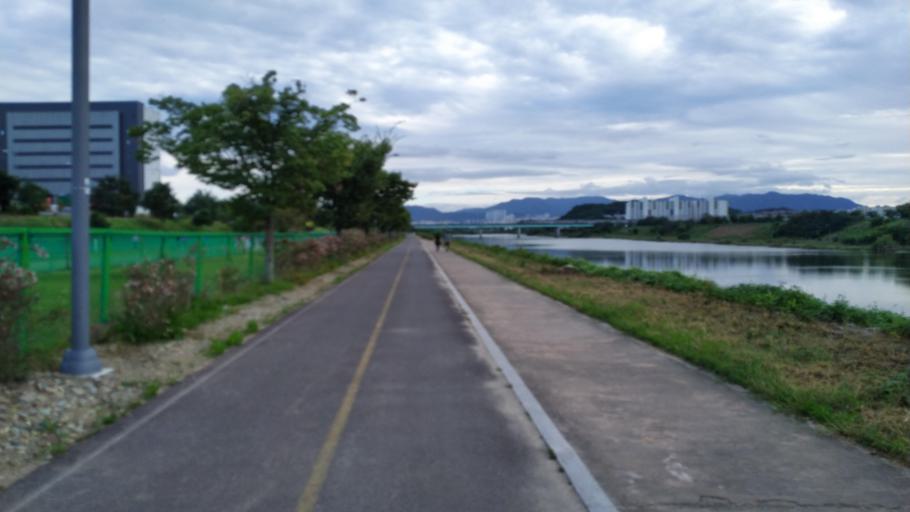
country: KR
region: Daegu
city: Daegu
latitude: 35.9254
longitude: 128.6324
